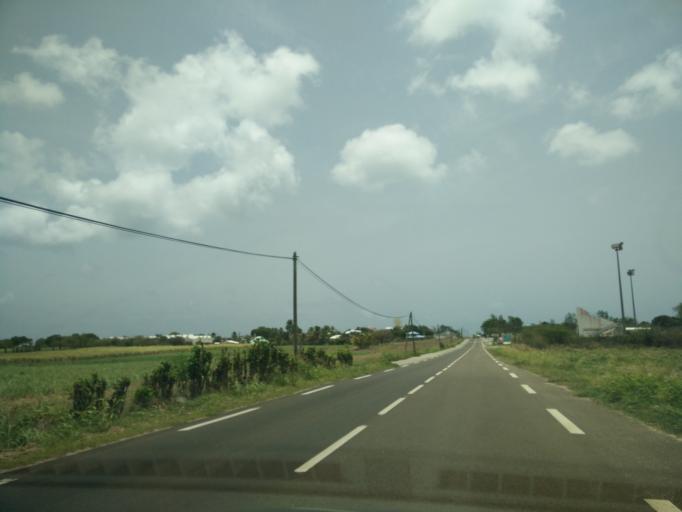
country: GP
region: Guadeloupe
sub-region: Guadeloupe
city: Anse-Bertrand
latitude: 16.4646
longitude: -61.5106
